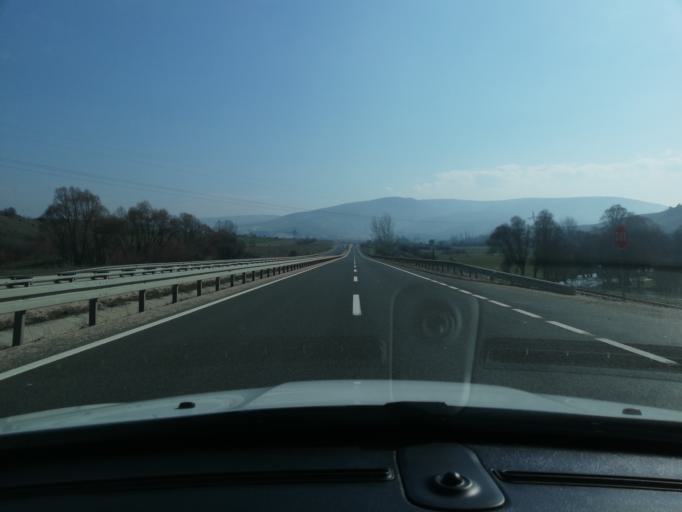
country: TR
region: Cankiri
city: Cerkes
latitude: 40.8368
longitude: 32.7458
